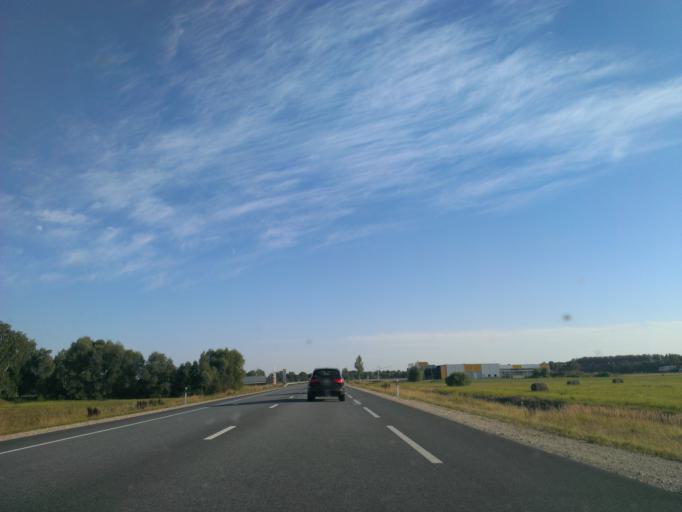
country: LV
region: Adazi
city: Adazi
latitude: 57.0919
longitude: 24.3127
